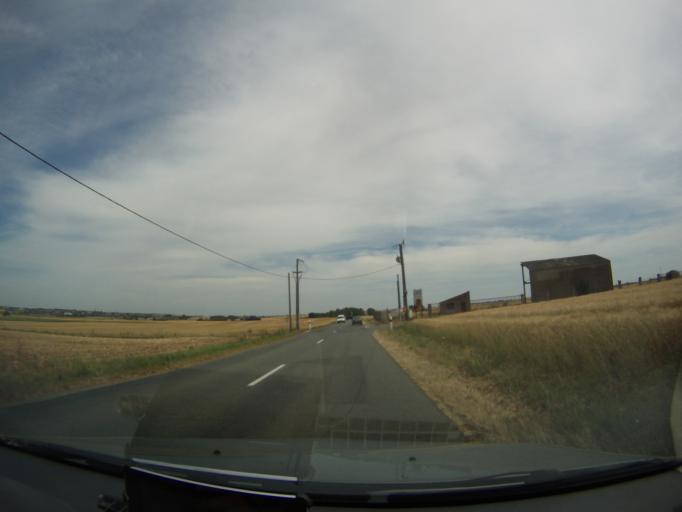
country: FR
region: Poitou-Charentes
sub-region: Departement de la Vienne
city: Mirebeau
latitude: 46.7859
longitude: 0.1259
